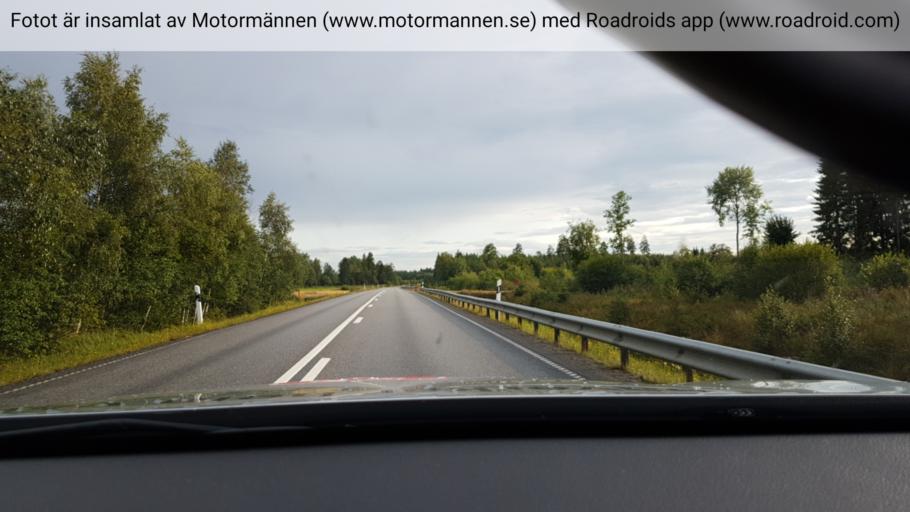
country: SE
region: Stockholm
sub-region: Norrtalje Kommun
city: Hallstavik
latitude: 60.0585
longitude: 18.5277
